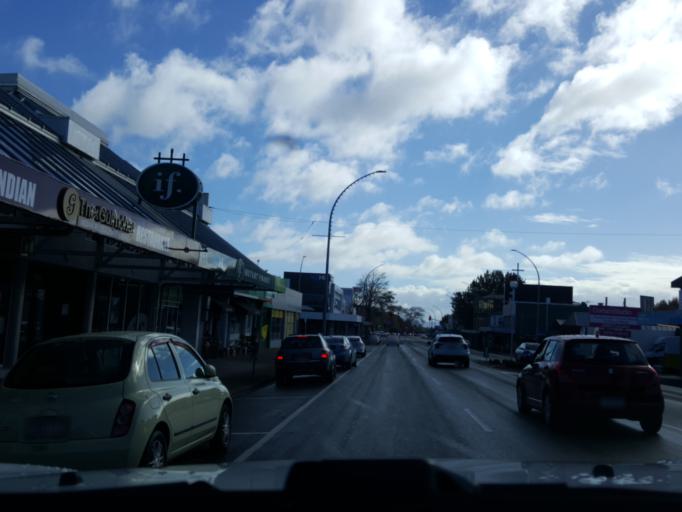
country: NZ
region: Waikato
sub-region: Hamilton City
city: Hamilton
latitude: -37.7812
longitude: 175.2774
